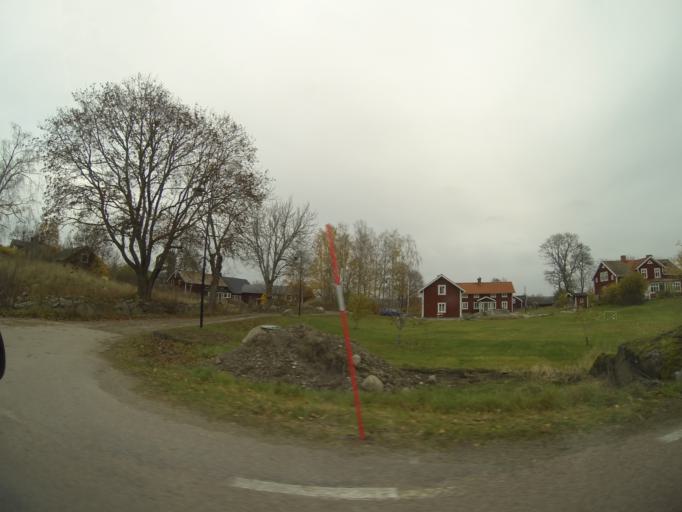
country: SE
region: Vaestmanland
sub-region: Vasteras
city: Vasteras
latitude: 59.6446
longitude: 16.4713
